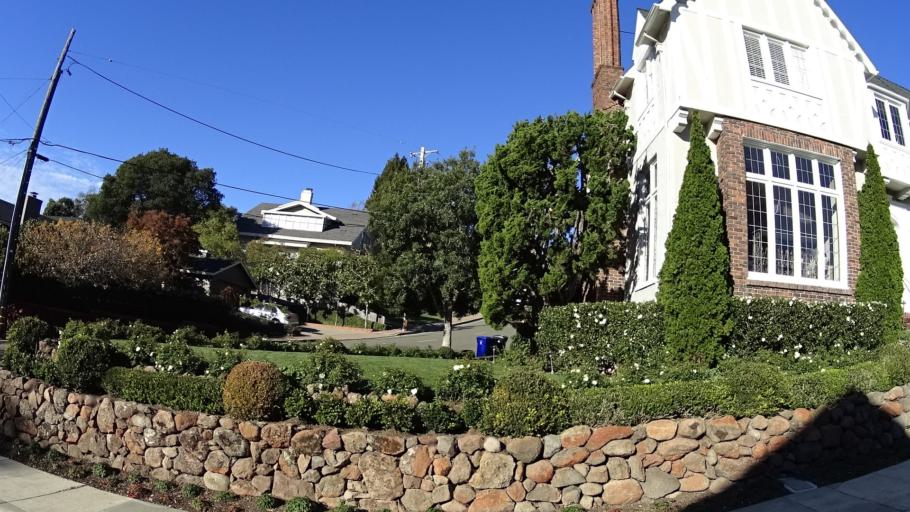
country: US
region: California
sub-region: Alameda County
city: Piedmont
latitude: 37.8223
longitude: -122.2271
